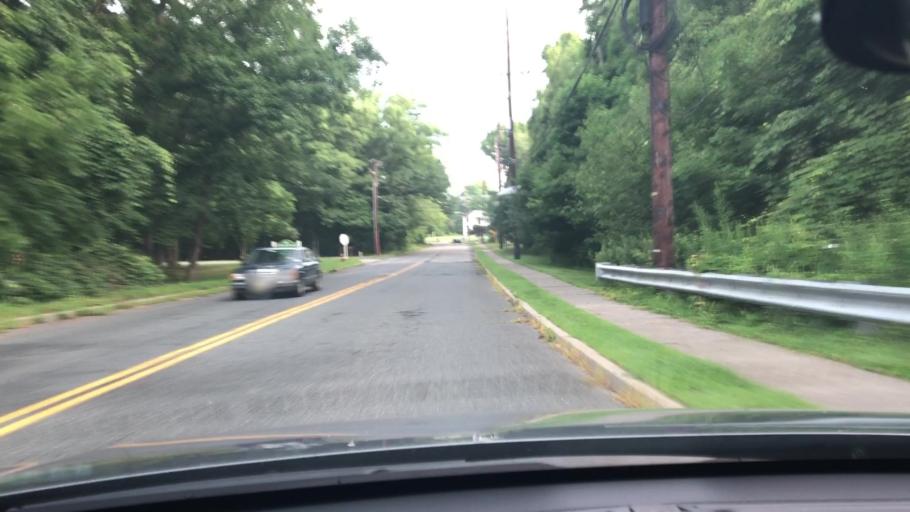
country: US
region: New Jersey
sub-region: Middlesex County
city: East Brunswick
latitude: 40.4264
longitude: -74.4446
